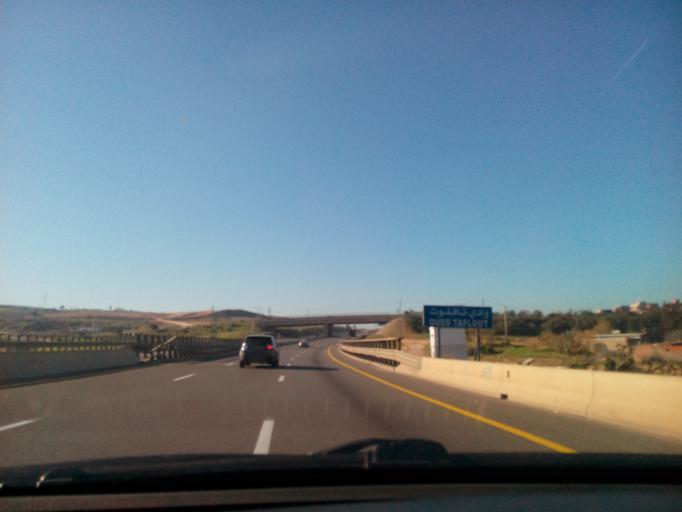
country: DZ
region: Chlef
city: Boukadir
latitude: 36.0583
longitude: 1.1461
